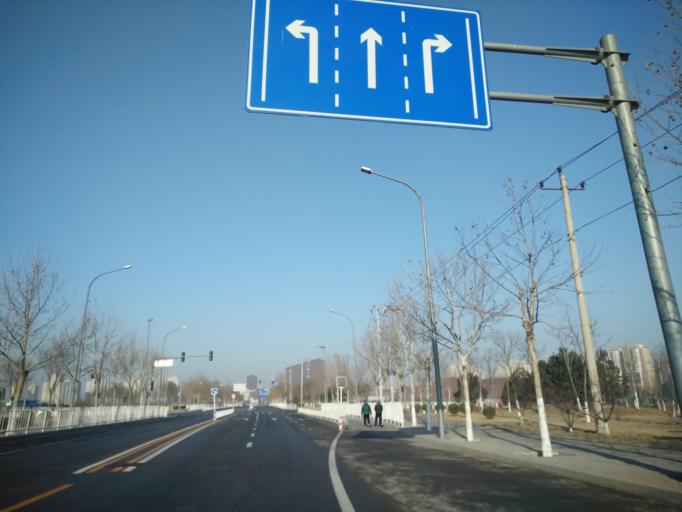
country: CN
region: Beijing
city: Yinghai
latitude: 39.7500
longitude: 116.4945
